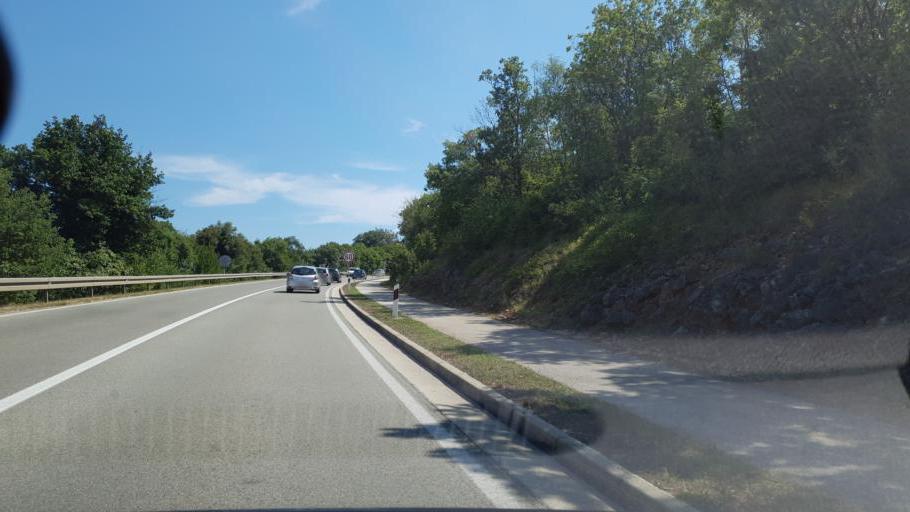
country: HR
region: Primorsko-Goranska
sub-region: Grad Krk
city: Krk
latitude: 45.0677
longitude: 14.5560
